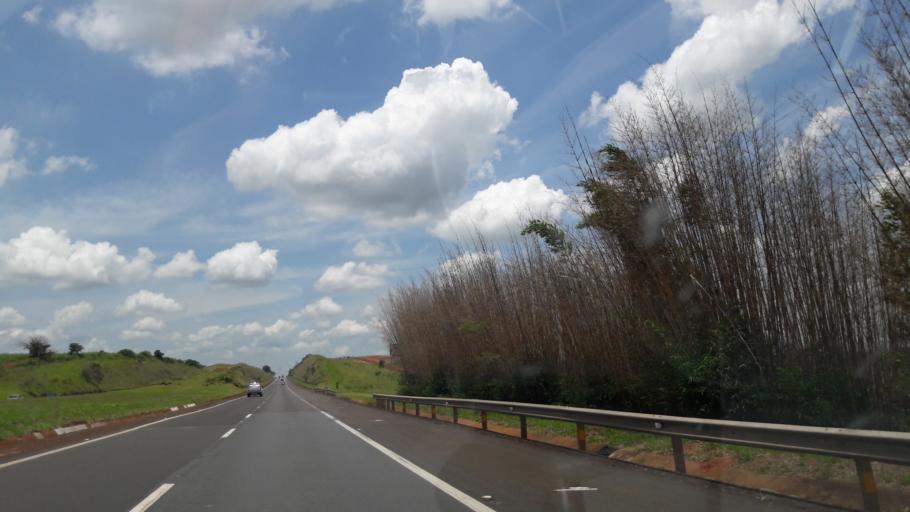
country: BR
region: Sao Paulo
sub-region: Avare
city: Avare
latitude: -22.9546
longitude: -48.8309
